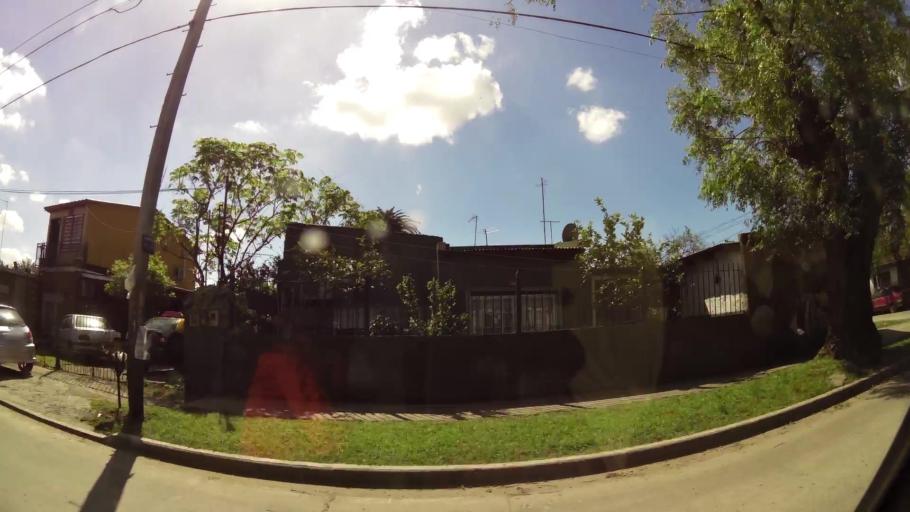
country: AR
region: Buenos Aires
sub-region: Partido de Quilmes
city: Quilmes
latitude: -34.8151
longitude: -58.2641
